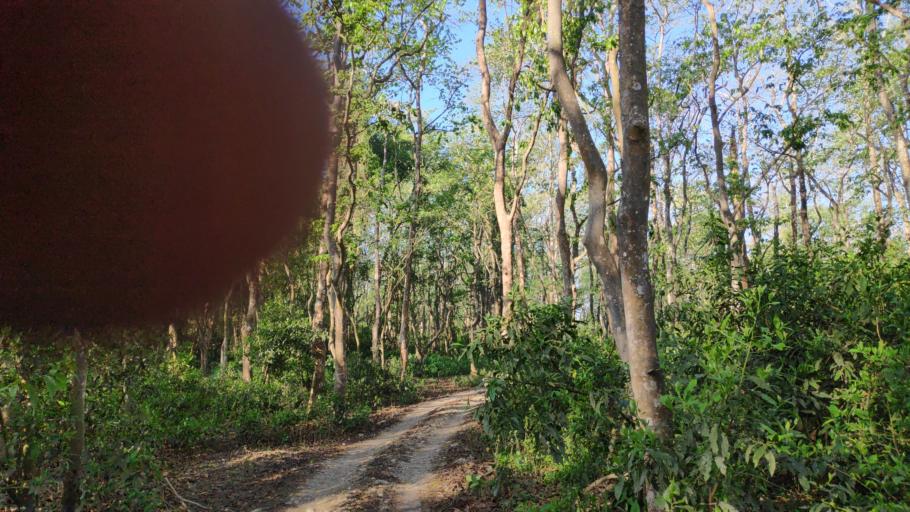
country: NP
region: Central Region
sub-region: Narayani Zone
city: Bharatpur
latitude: 27.5597
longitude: 84.5663
